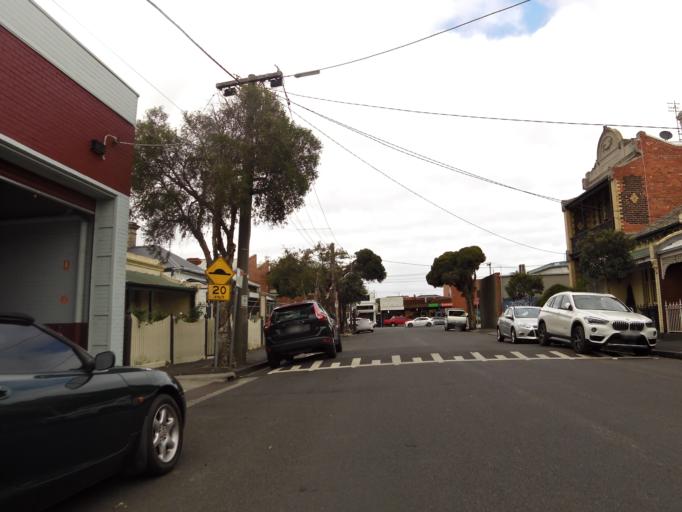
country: AU
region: Victoria
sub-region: Yarra
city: Richmond
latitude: -37.8102
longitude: 145.0034
